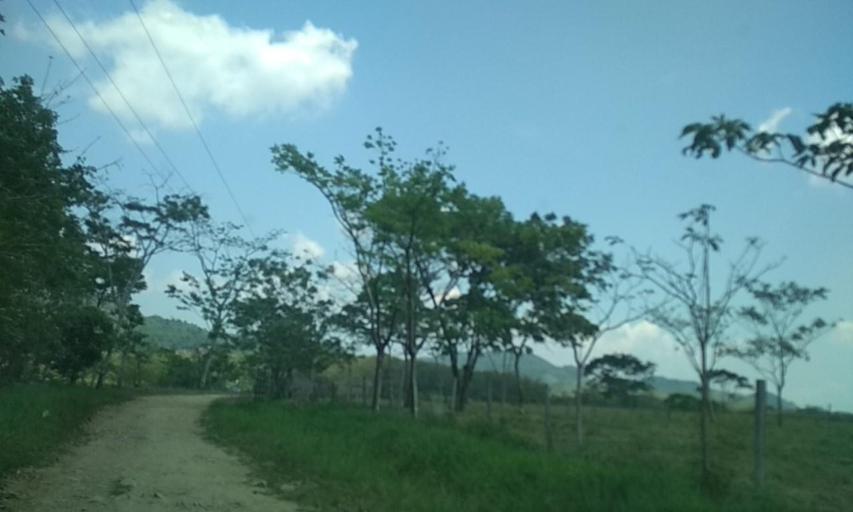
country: MX
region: Chiapas
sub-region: Tecpatan
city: Raudales Malpaso
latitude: 17.3002
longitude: -93.8168
